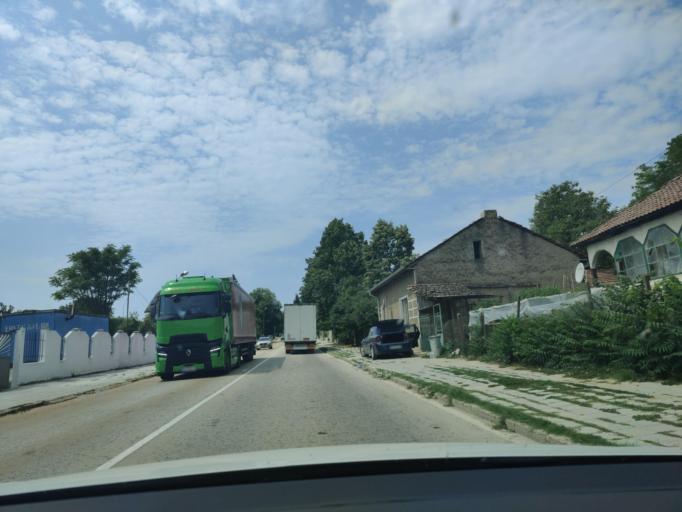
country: BG
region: Vidin
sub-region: Obshtina Dimovo
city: Dimovo
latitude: 43.7475
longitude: 22.7339
